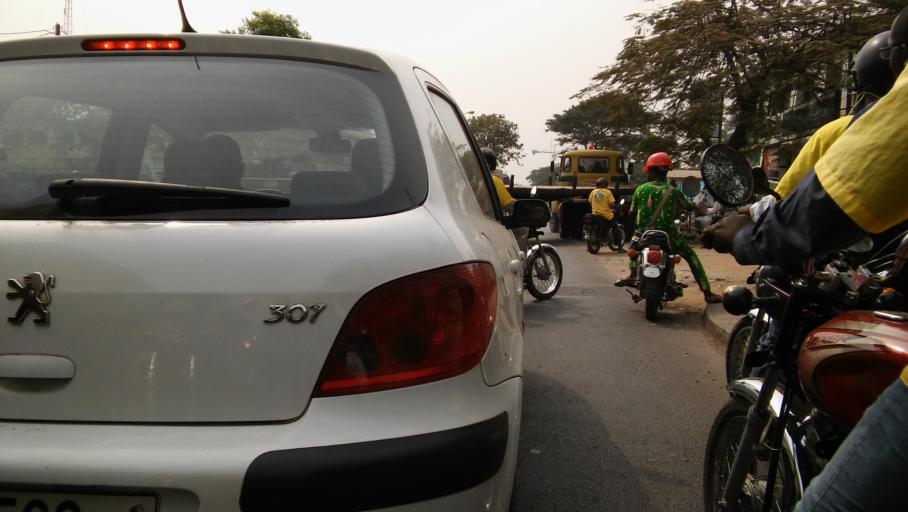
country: BJ
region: Littoral
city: Cotonou
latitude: 6.3511
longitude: 2.4256
